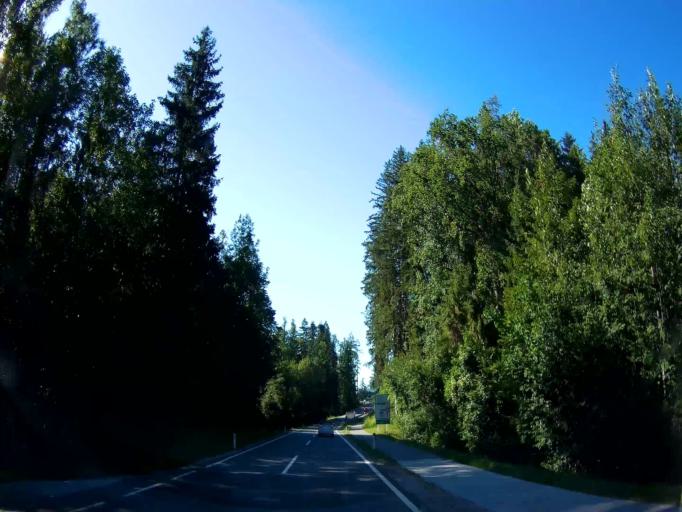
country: AT
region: Salzburg
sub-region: Politischer Bezirk Hallein
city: Adnet
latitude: 47.6596
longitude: 13.1249
